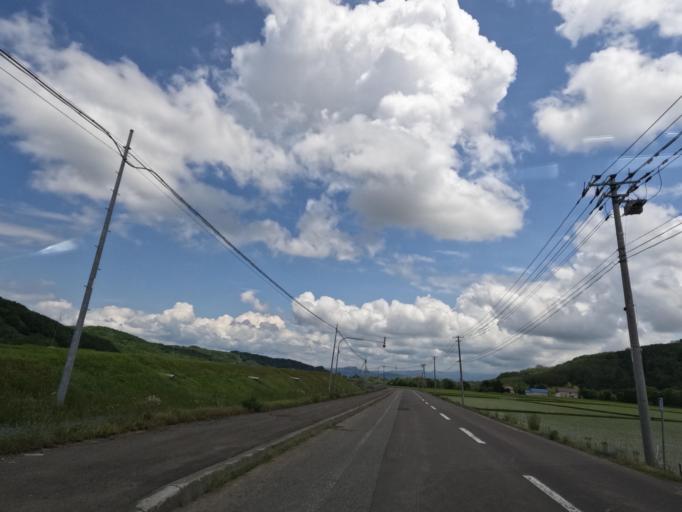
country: JP
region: Hokkaido
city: Takikawa
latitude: 43.5840
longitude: 141.8048
